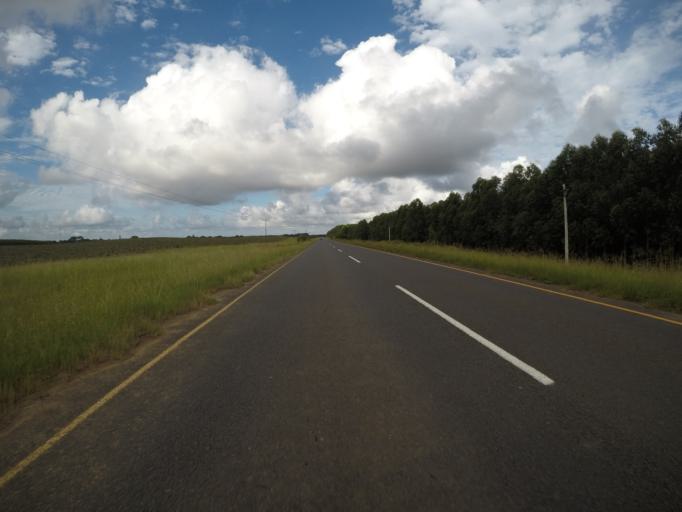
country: ZA
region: KwaZulu-Natal
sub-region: uMkhanyakude District Municipality
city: Mtubatuba
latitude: -28.3858
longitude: 32.2364
